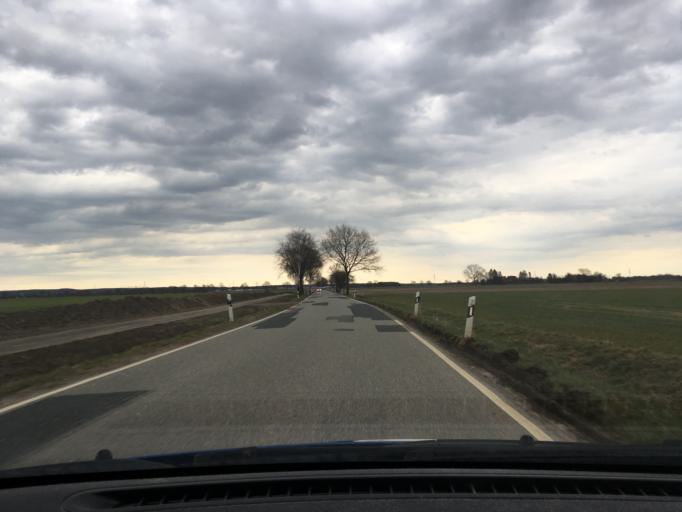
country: DE
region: Lower Saxony
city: Handorf
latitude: 53.3757
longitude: 10.3114
